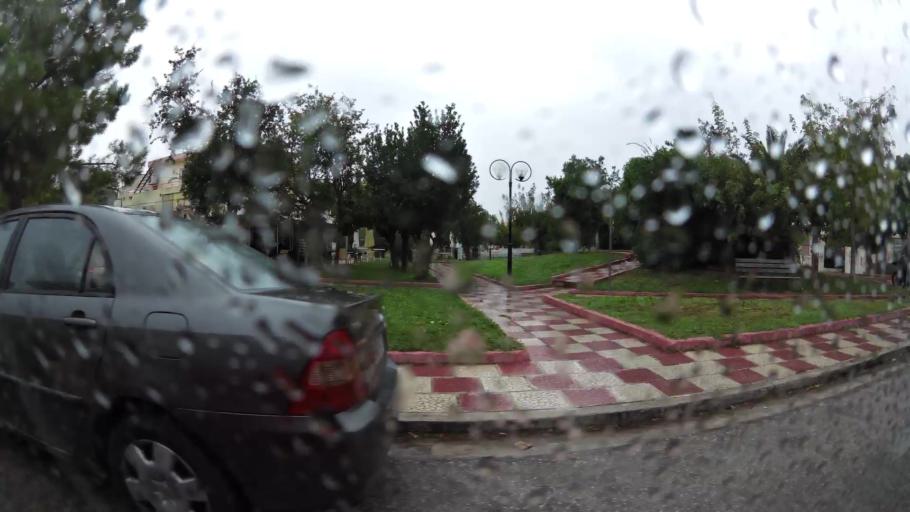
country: GR
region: Attica
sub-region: Nomarchia Athinas
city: Agioi Anargyroi
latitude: 38.0220
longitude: 23.7196
